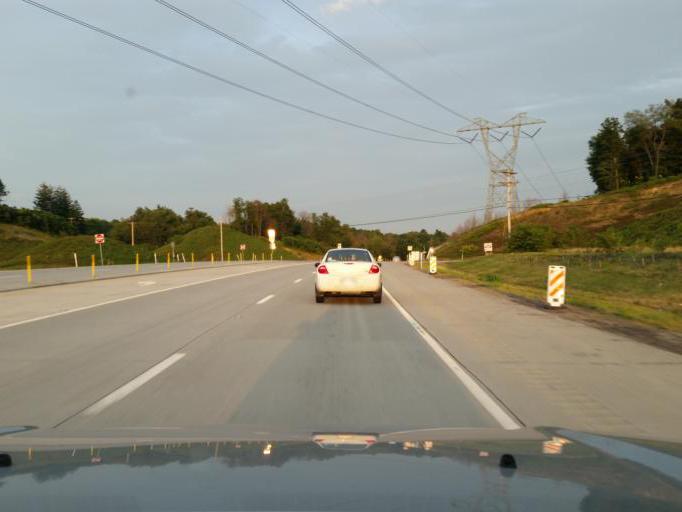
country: US
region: Pennsylvania
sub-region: Indiana County
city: Black Lick
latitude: 40.4546
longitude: -79.1250
